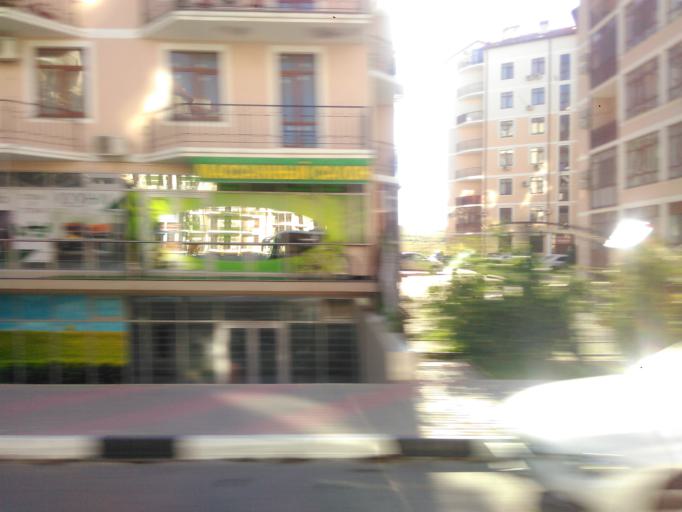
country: RU
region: Krasnodarskiy
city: Gelendzhik
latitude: 44.5494
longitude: 38.0605
